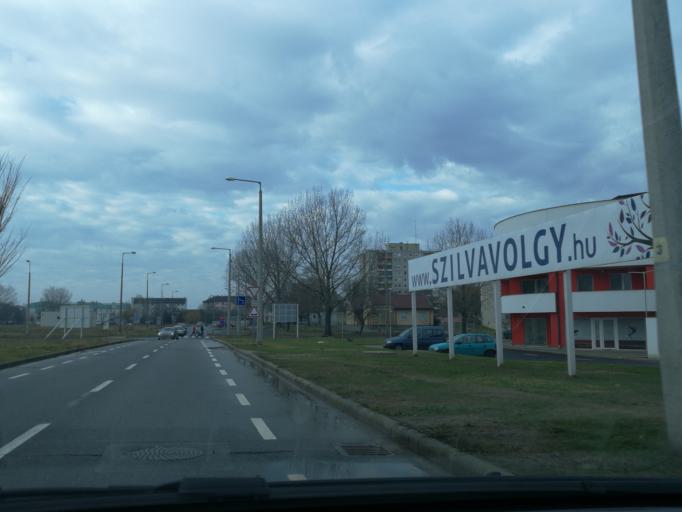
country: HU
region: Szabolcs-Szatmar-Bereg
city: Nyiregyhaza
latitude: 47.9555
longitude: 21.7450
